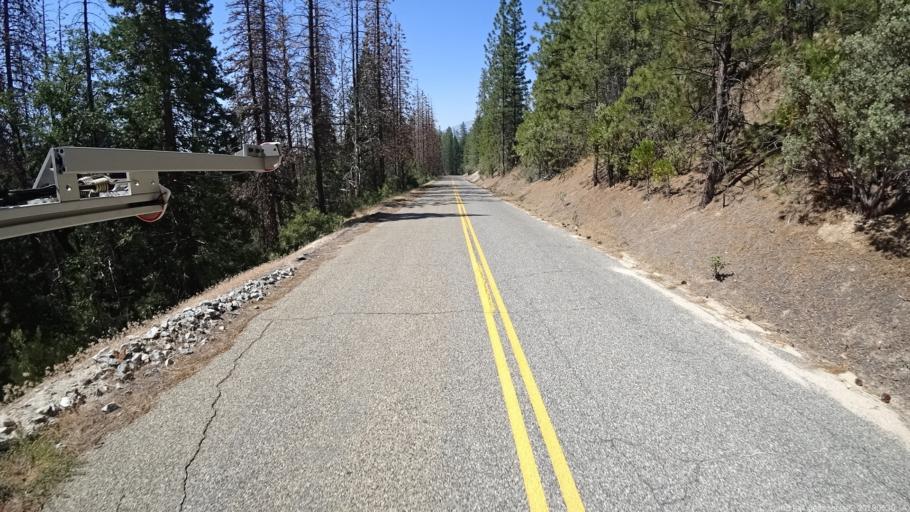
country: US
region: California
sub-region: Madera County
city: Oakhurst
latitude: 37.3989
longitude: -119.3506
